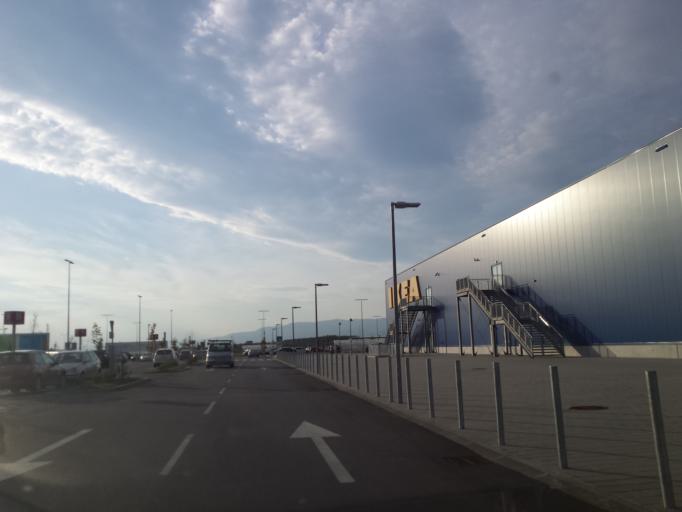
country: HR
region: Grad Zagreb
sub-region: Sesvete
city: Sesvete
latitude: 45.7913
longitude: 16.1560
